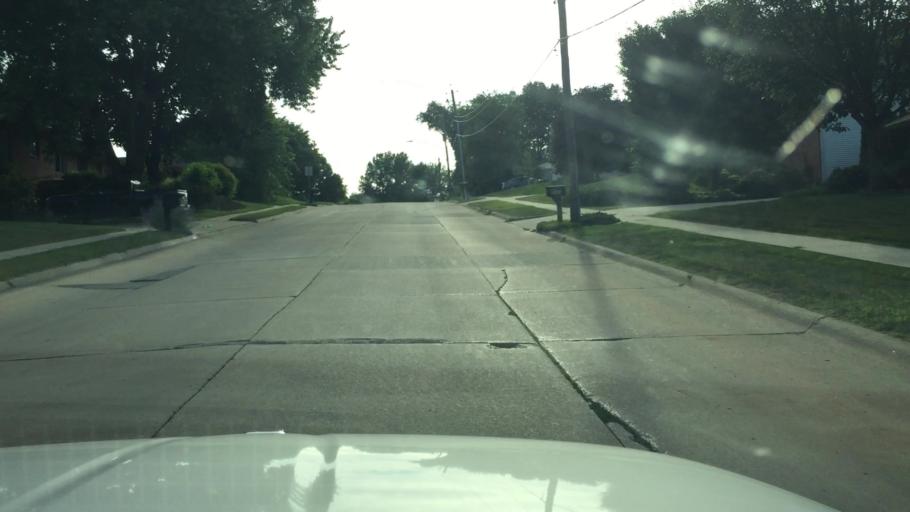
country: US
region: Iowa
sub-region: Johnson County
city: Iowa City
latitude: 41.6605
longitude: -91.5000
